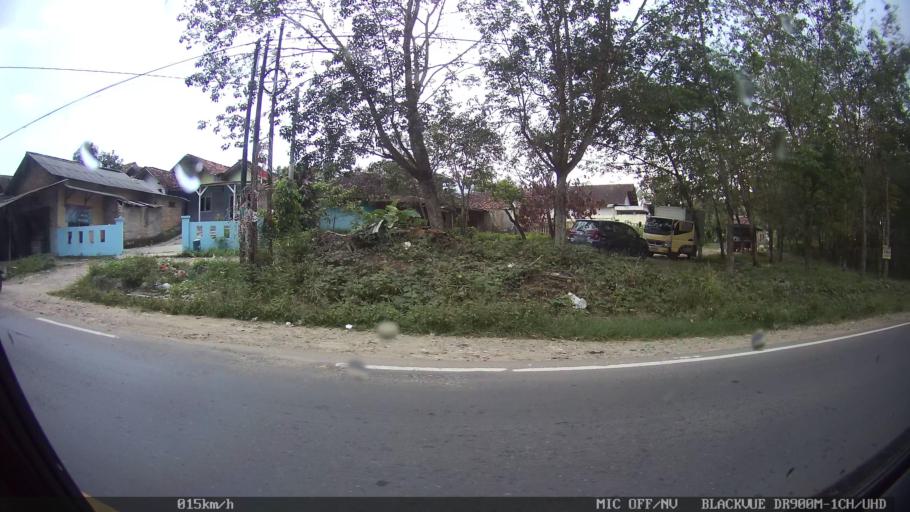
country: ID
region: Lampung
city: Gedongtataan
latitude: -5.3688
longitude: 105.1363
